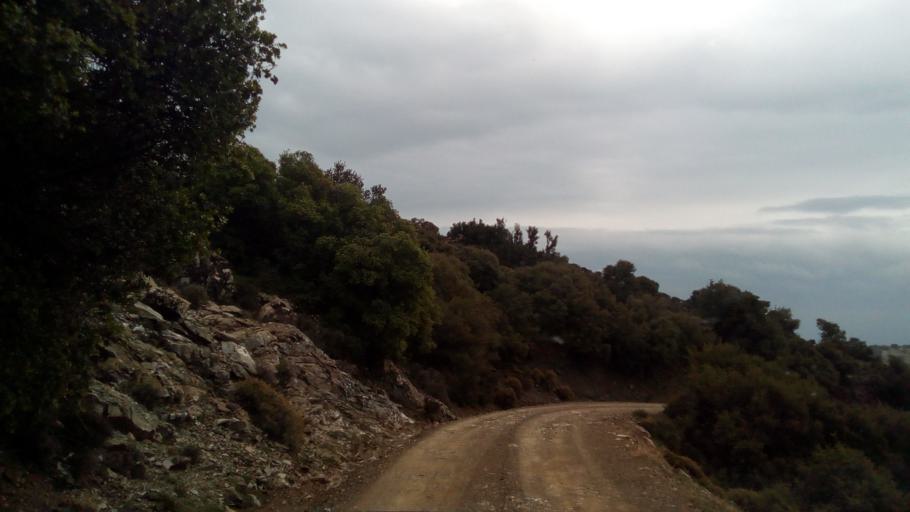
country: GR
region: West Greece
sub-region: Nomos Achaias
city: Selianitika
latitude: 38.4105
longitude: 22.0895
